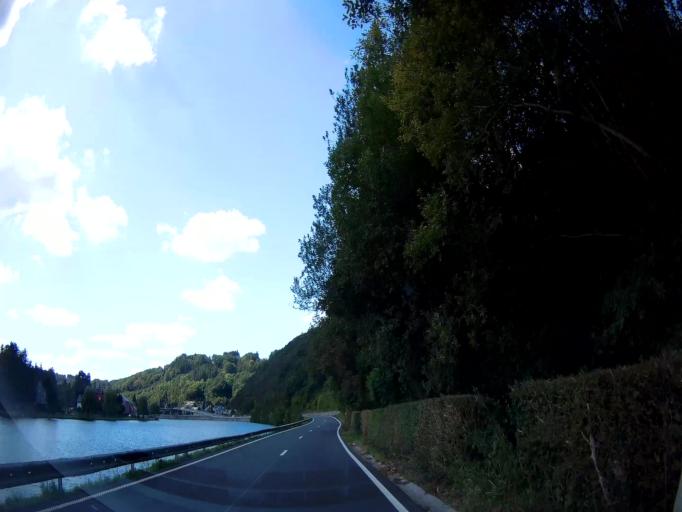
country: BE
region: Wallonia
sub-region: Province de Namur
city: Hastiere-Lavaux
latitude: 50.2170
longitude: 4.8356
